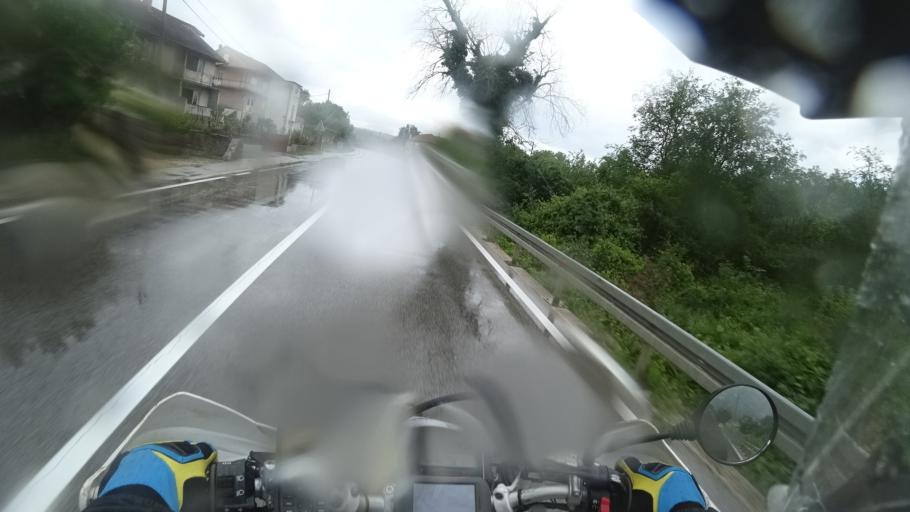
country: HR
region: Sibensko-Kniniska
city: Knin
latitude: 44.0433
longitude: 16.2235
